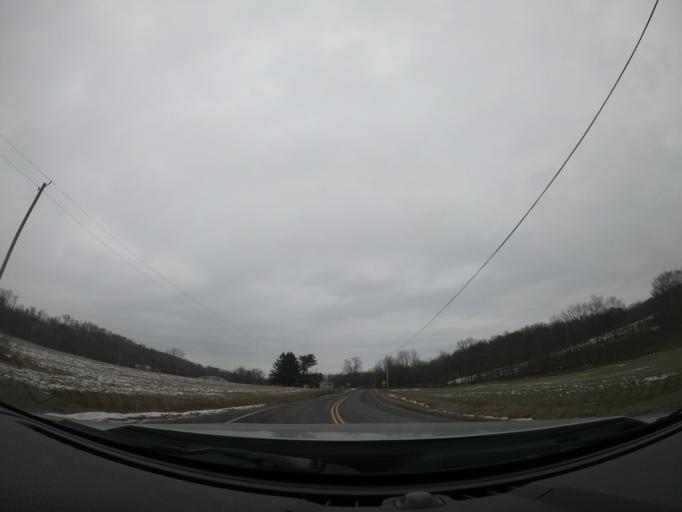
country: US
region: New York
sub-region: Cayuga County
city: Moravia
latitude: 42.6406
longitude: -76.4499
